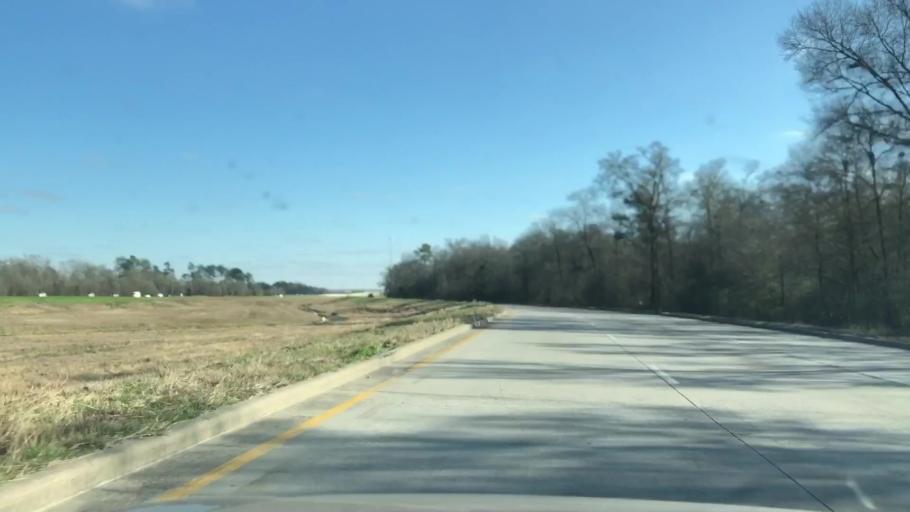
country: US
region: Texas
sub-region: Harris County
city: Cloverleaf
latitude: 29.8234
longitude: -95.1948
